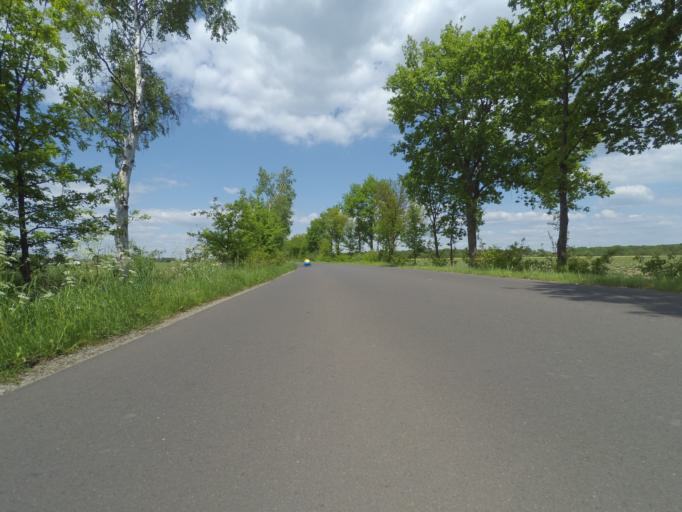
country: DE
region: Lower Saxony
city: Muden
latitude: 52.5047
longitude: 10.3670
